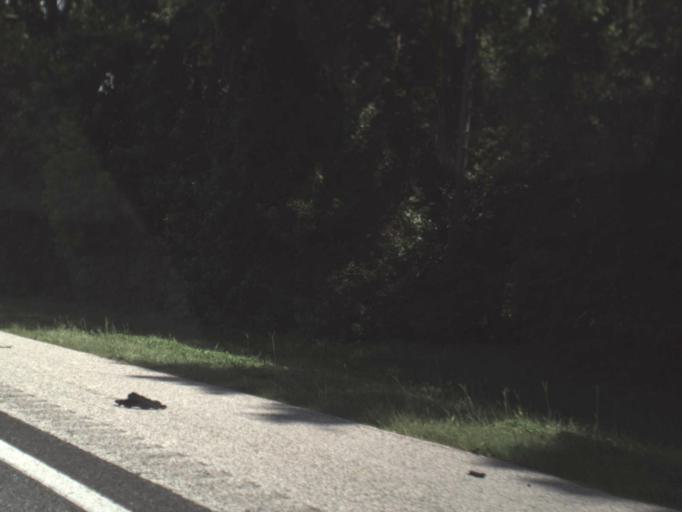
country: US
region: Florida
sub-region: Alachua County
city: Alachua
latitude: 29.7405
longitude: -82.4793
